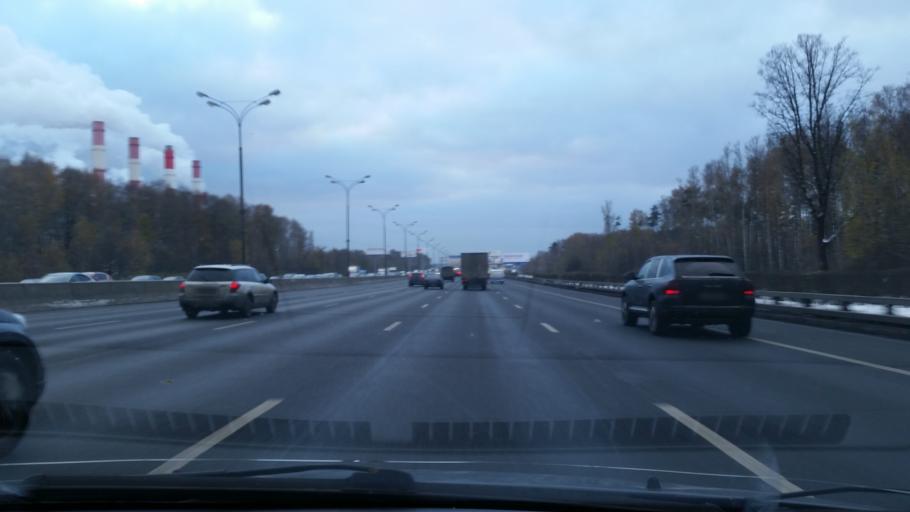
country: RU
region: Moscow
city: Businovo
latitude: 55.9008
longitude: 37.5158
